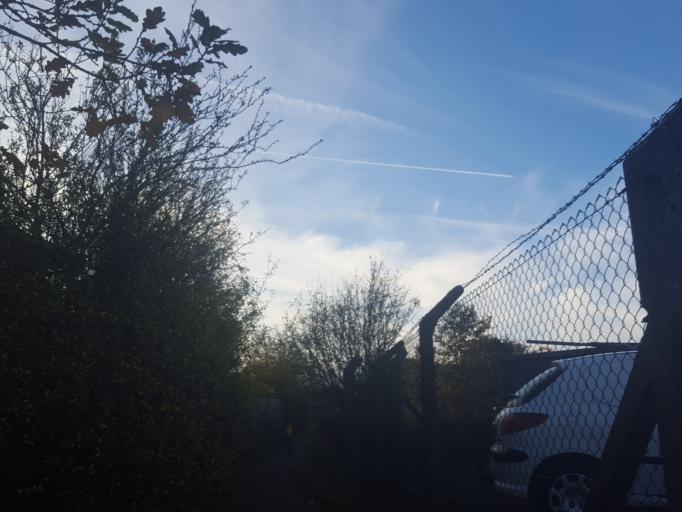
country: GB
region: England
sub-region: Essex
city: Little Clacton
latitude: 51.8163
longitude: 1.1701
